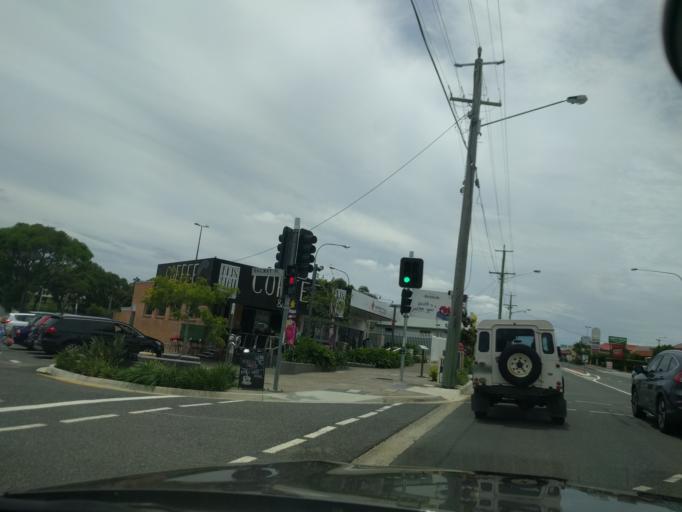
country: AU
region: Queensland
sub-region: Brisbane
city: Grange
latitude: -27.4235
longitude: 153.0002
